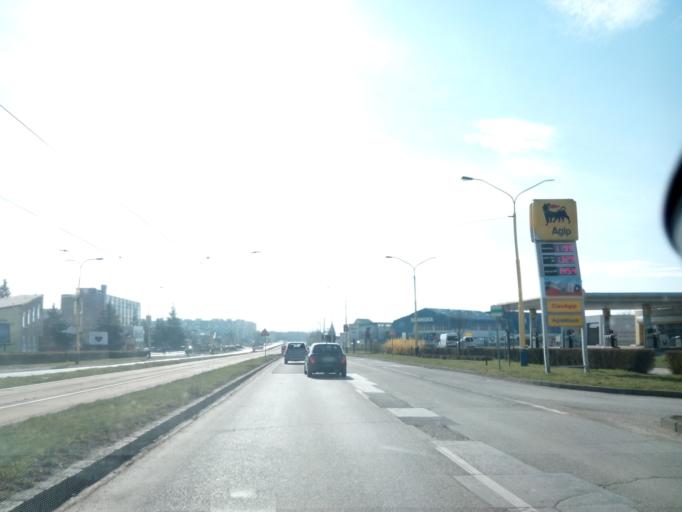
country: SK
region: Kosicky
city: Kosice
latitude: 48.7039
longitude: 21.2449
